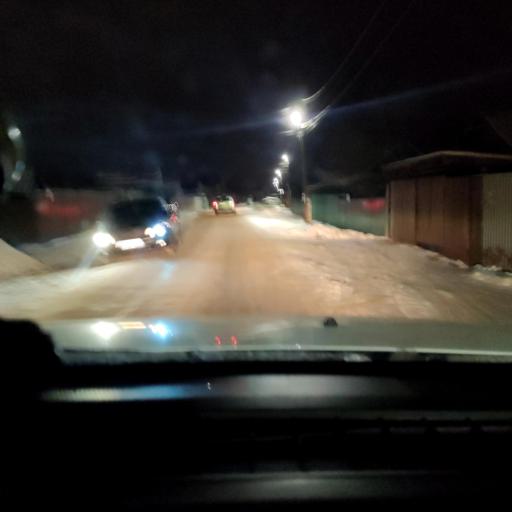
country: RU
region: Samara
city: Samara
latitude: 53.1357
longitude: 50.1000
